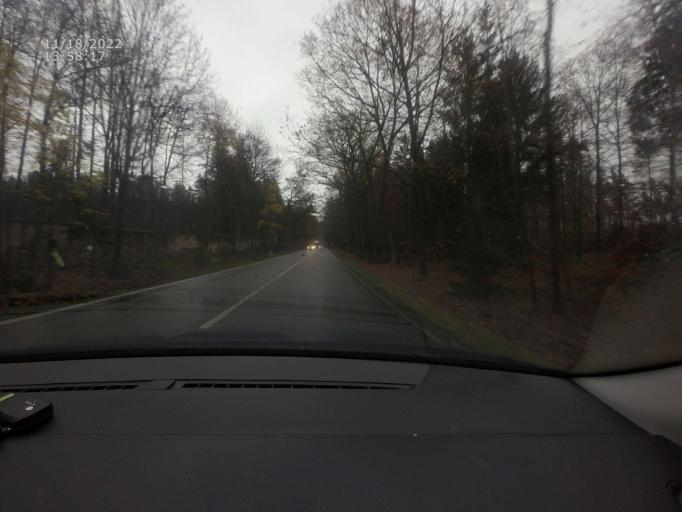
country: CZ
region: Jihocesky
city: Sedlice
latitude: 49.3643
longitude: 13.9795
